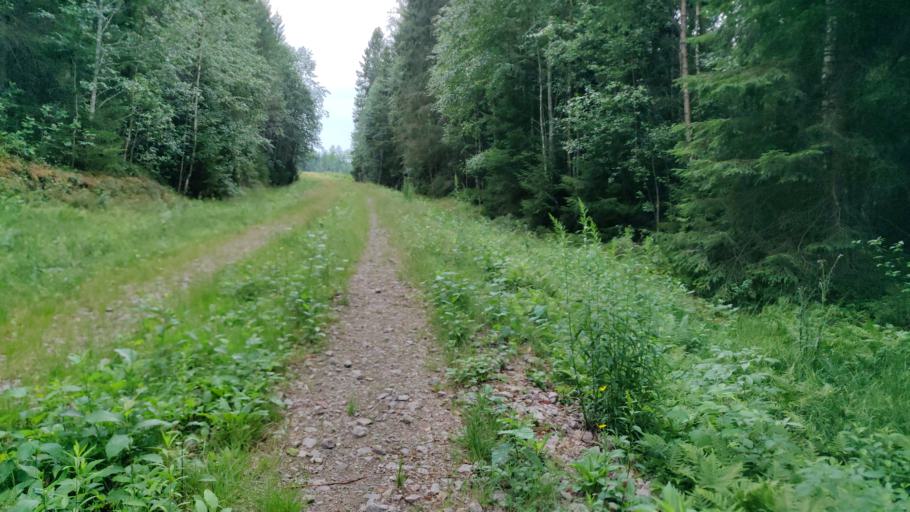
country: SE
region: Vaermland
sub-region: Hagfors Kommun
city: Hagfors
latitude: 59.9656
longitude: 13.5729
